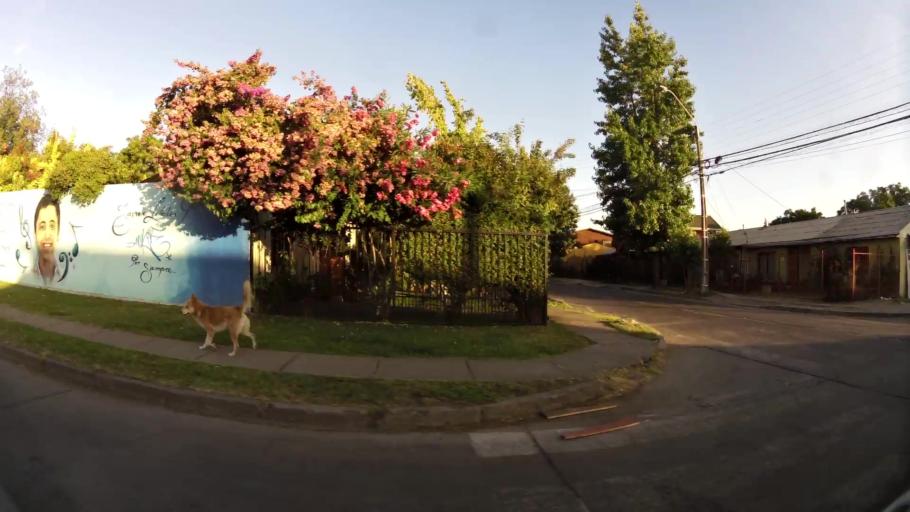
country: CL
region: Maule
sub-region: Provincia de Talca
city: Talca
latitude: -35.4442
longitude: -71.6792
